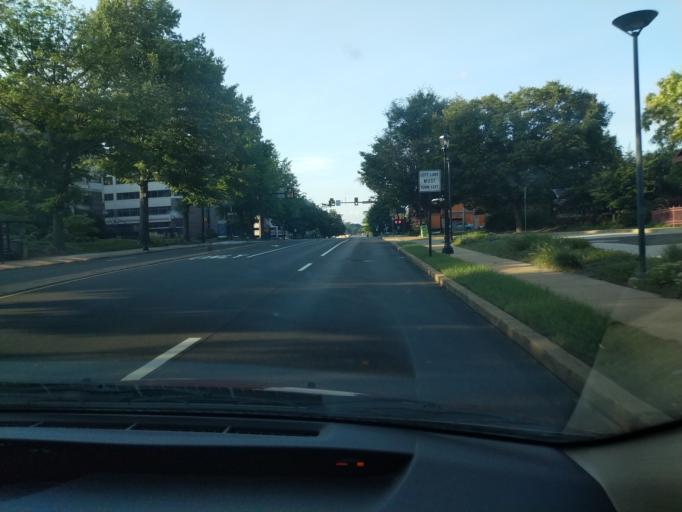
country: US
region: Pennsylvania
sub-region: Montgomery County
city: Jenkintown
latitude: 40.1184
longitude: -75.1196
